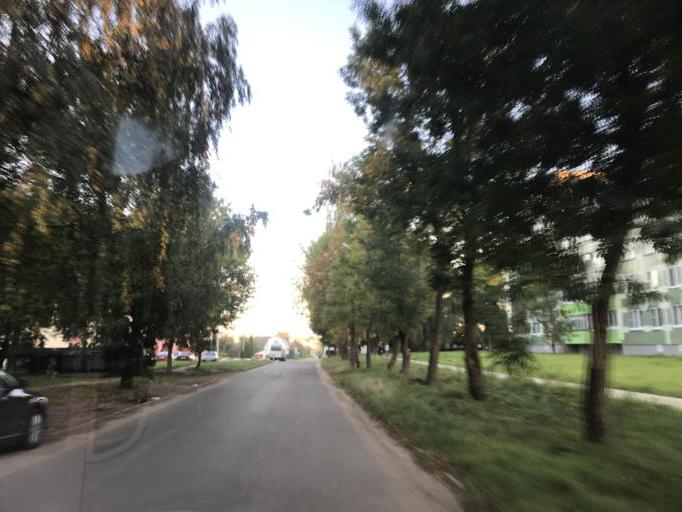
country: BY
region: Mogilev
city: Mahilyow
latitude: 53.9067
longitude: 30.3211
